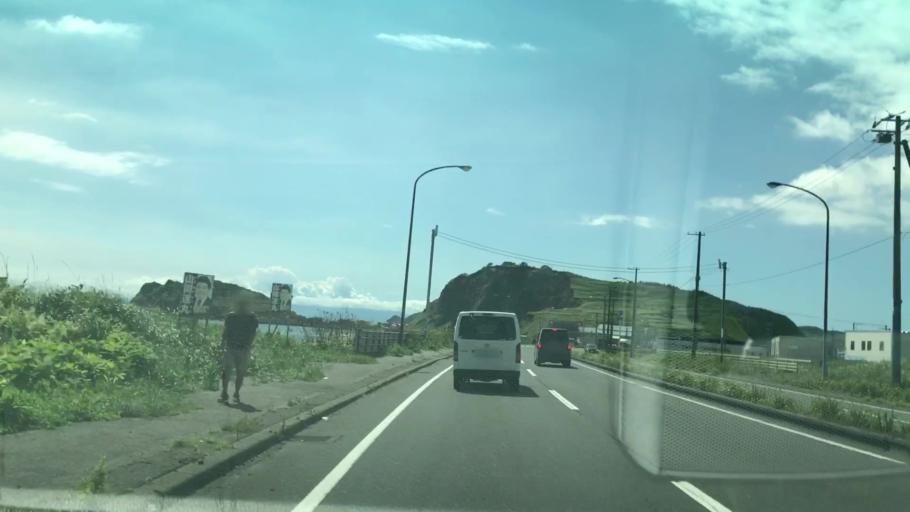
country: JP
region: Hokkaido
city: Muroran
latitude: 42.3459
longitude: 141.0375
